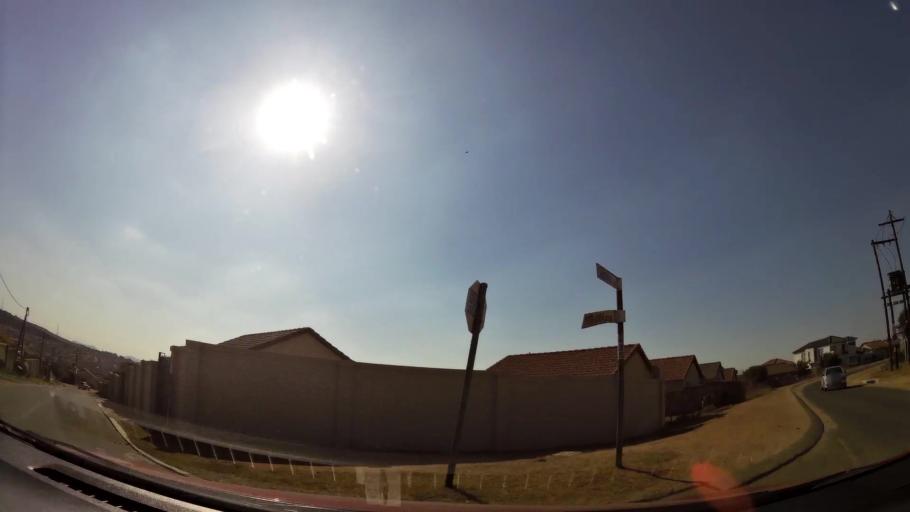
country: ZA
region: Gauteng
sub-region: West Rand District Municipality
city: Muldersdriseloop
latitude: -26.0367
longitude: 27.9254
